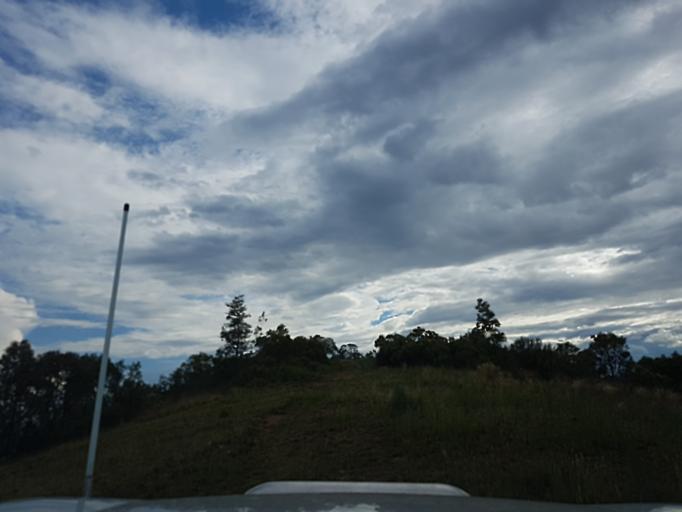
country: AU
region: New South Wales
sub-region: Snowy River
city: Jindabyne
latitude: -36.9977
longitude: 148.4053
